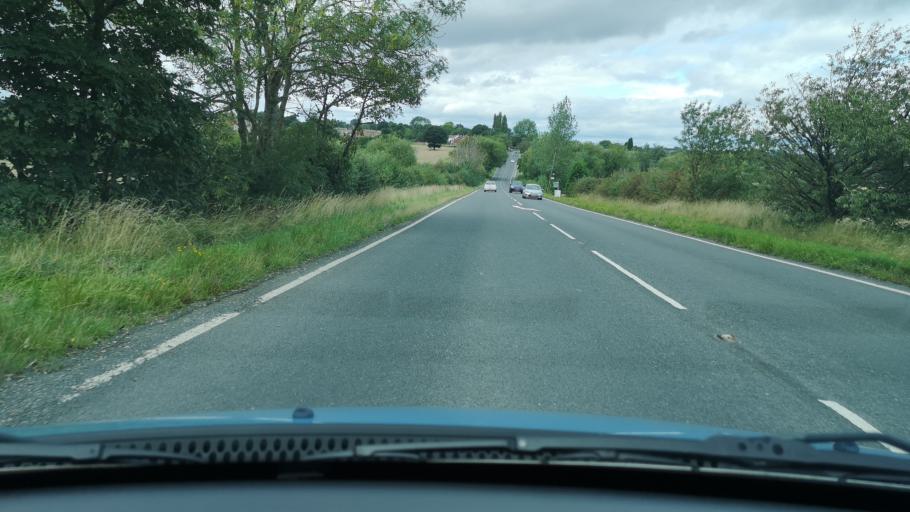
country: GB
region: England
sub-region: City and Borough of Wakefield
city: Low Ackworth
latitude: 53.6357
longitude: -1.3265
